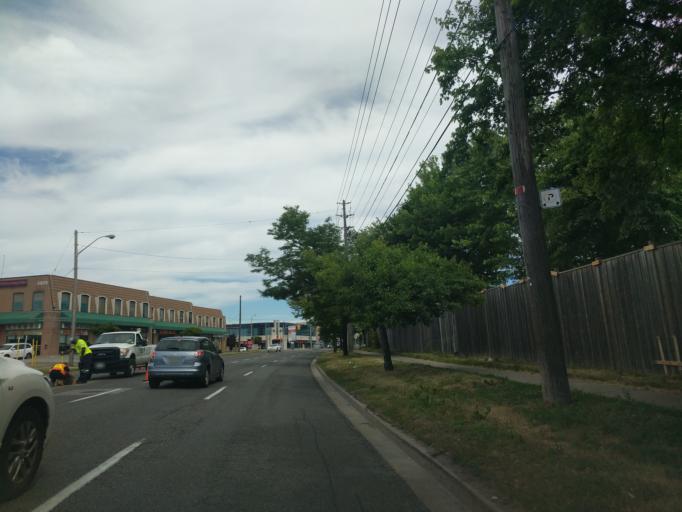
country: CA
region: Ontario
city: Scarborough
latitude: 43.8060
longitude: -79.2879
